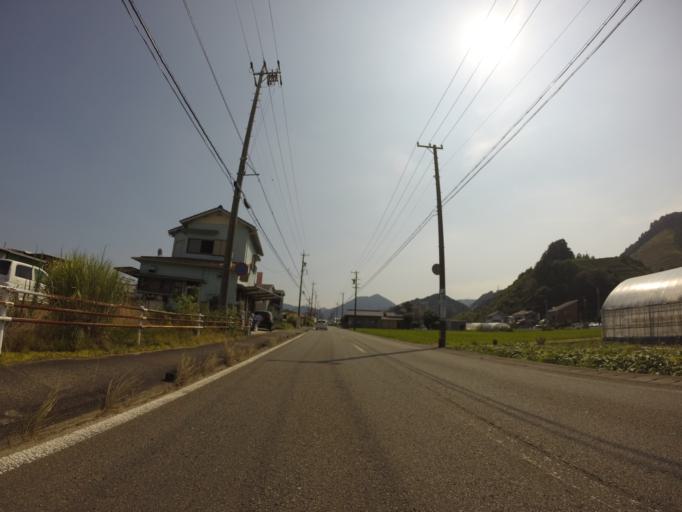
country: JP
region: Shizuoka
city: Shizuoka-shi
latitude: 35.0325
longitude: 138.3670
